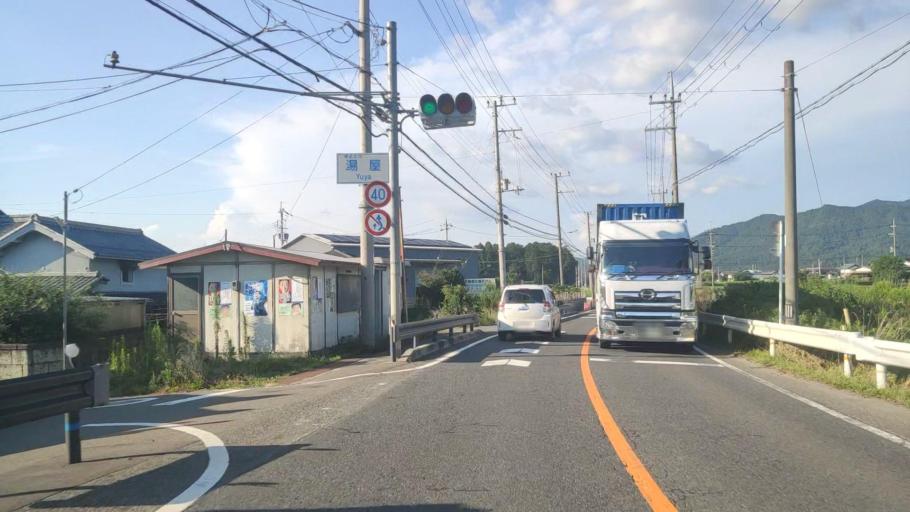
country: JP
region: Shiga Prefecture
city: Youkaichi
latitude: 35.1403
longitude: 136.2623
